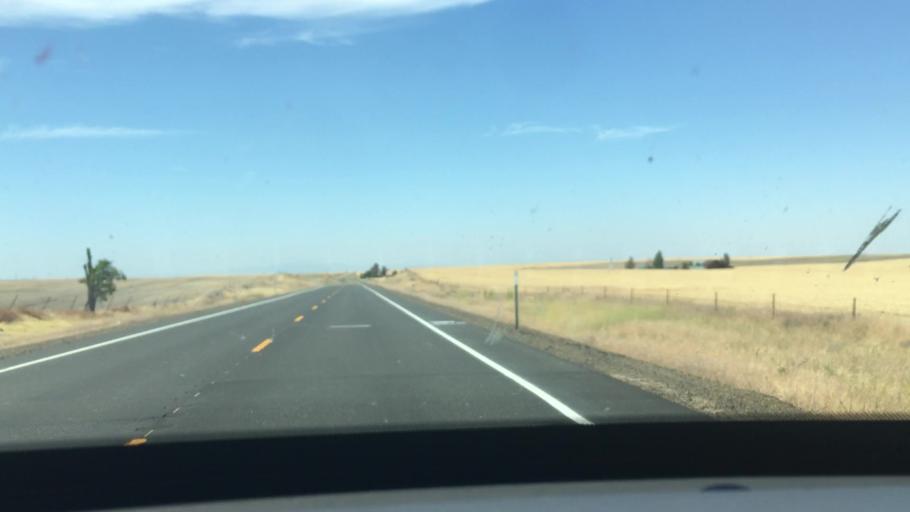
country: US
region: Oregon
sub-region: Sherman County
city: Moro
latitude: 45.3235
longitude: -120.7687
